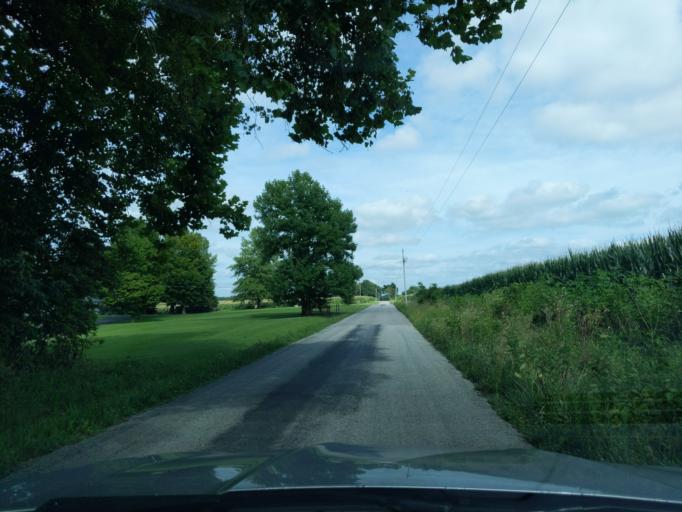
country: US
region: Indiana
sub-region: Decatur County
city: Greensburg
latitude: 39.2350
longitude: -85.3923
